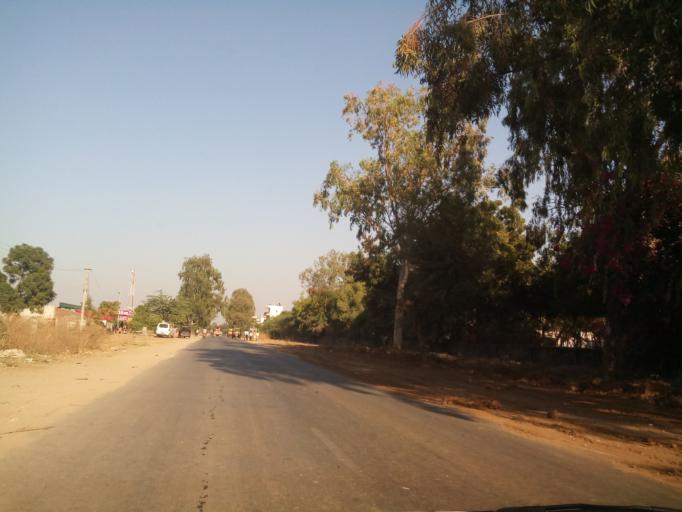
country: IN
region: Rajasthan
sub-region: Sirohi
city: Abu Road
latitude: 24.5382
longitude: 72.8029
